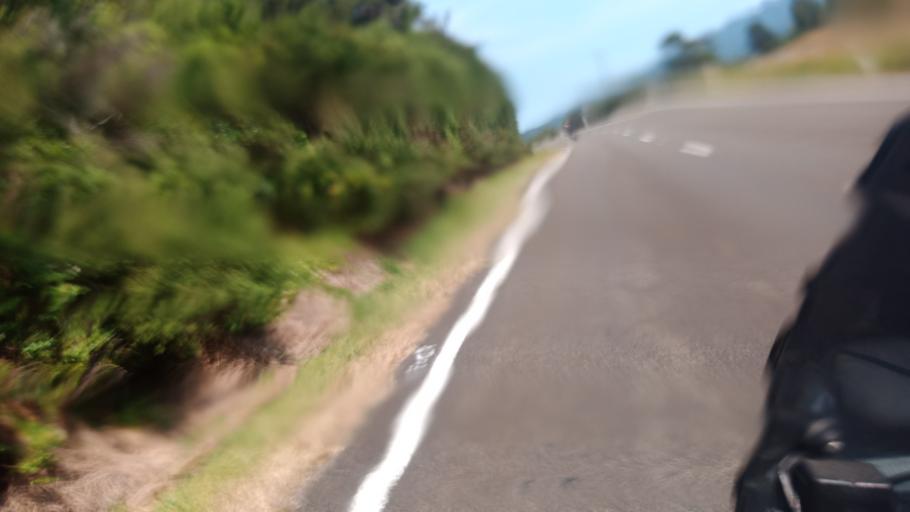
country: NZ
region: Bay of Plenty
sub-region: Opotiki District
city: Opotiki
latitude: -37.6027
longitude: 178.2743
